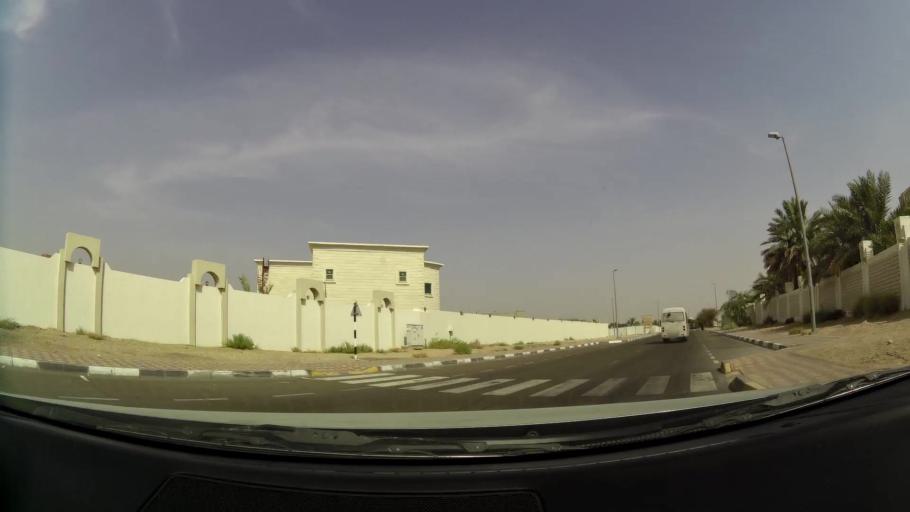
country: AE
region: Abu Dhabi
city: Al Ain
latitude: 24.1471
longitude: 55.6994
